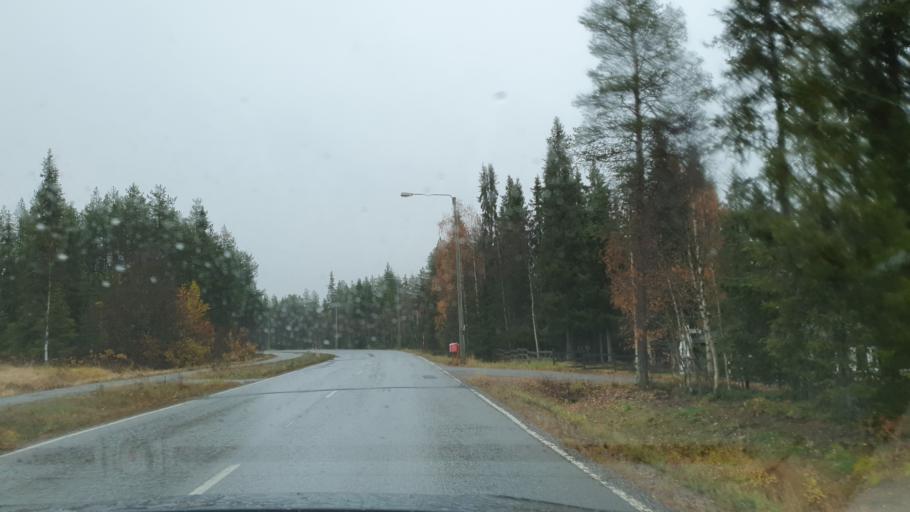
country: FI
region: Lapland
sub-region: Tunturi-Lappi
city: Kolari
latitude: 67.6027
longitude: 24.1343
